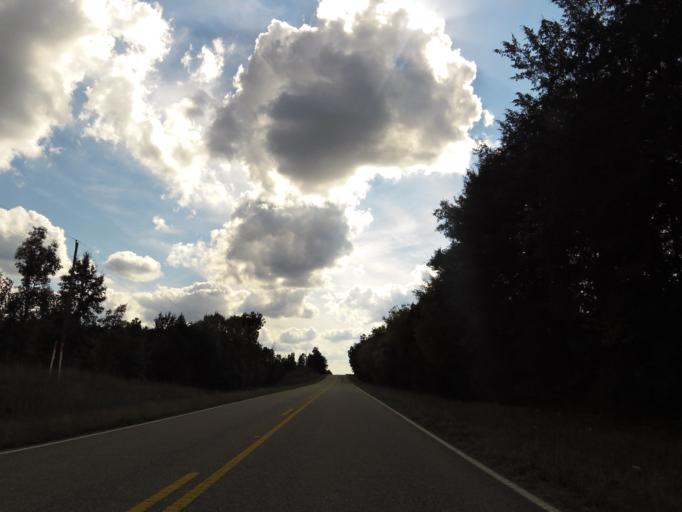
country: US
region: Alabama
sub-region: Dallas County
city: Selmont-West Selmont
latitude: 32.2156
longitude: -87.0033
